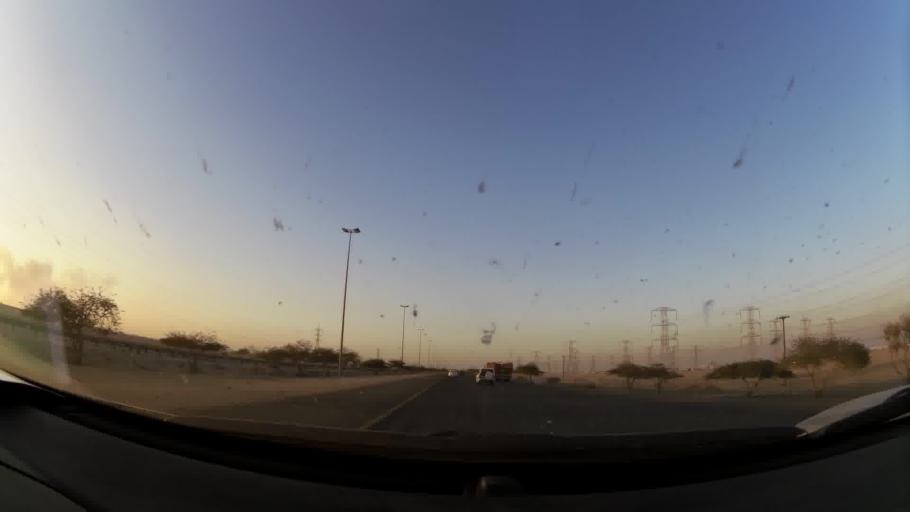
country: KW
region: Al Ahmadi
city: Al Ahmadi
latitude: 28.9748
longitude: 48.1119
